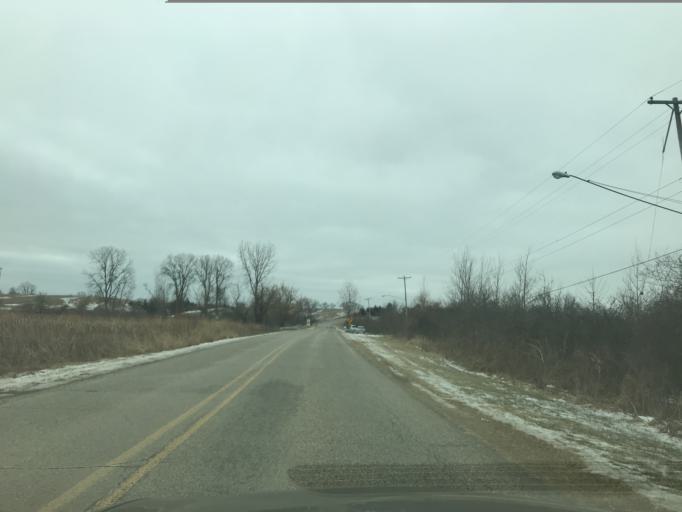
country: US
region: Michigan
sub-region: Jackson County
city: Brooklyn
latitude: 42.0620
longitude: -84.3255
